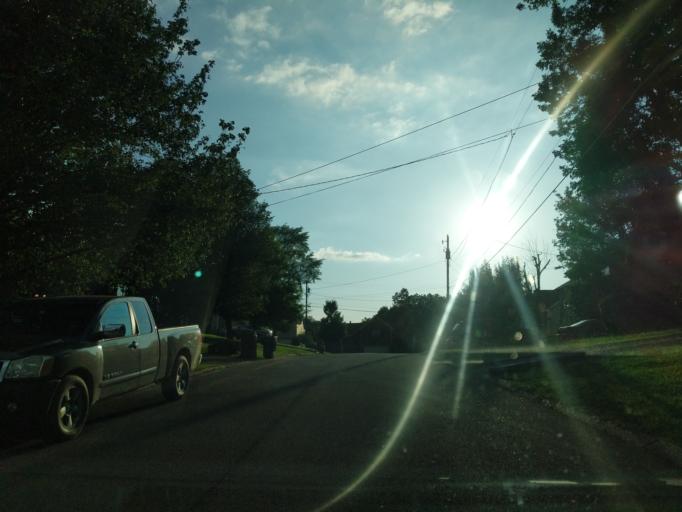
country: US
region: Tennessee
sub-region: Sumner County
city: Hendersonville
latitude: 36.2956
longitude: -86.6392
